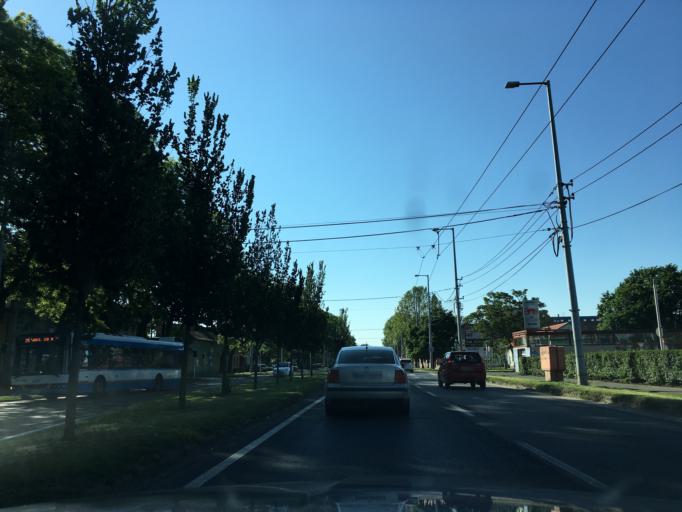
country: HU
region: Hajdu-Bihar
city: Debrecen
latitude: 47.5285
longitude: 21.6141
